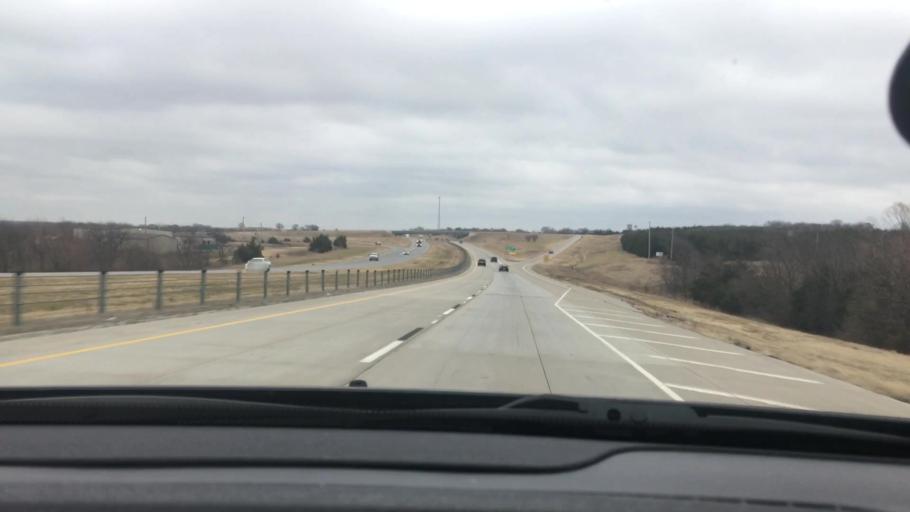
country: US
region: Oklahoma
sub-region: Bryan County
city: Durant
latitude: 34.1263
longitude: -96.2799
